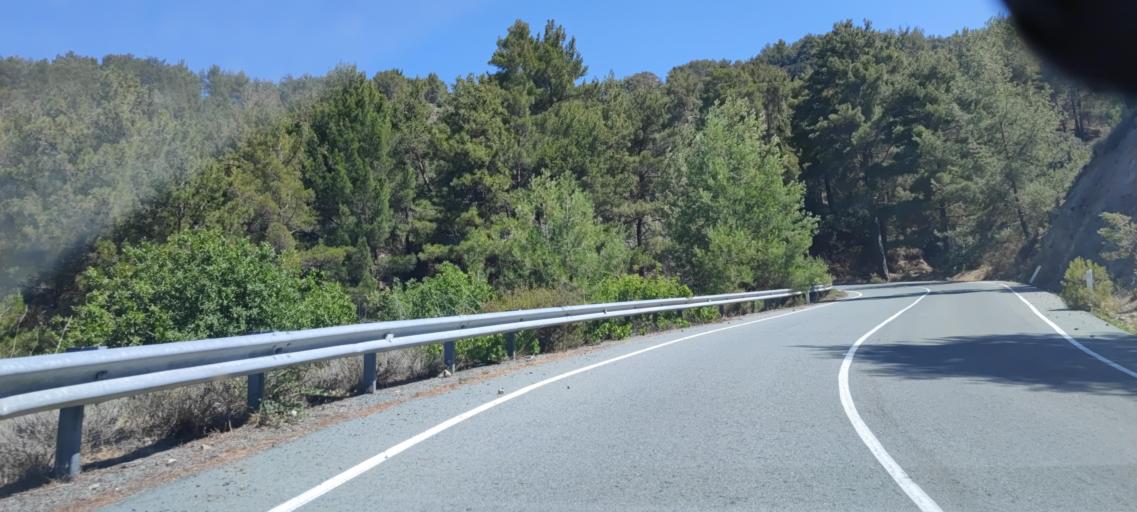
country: CY
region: Lefkosia
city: Kakopetria
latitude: 34.9115
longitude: 32.8171
